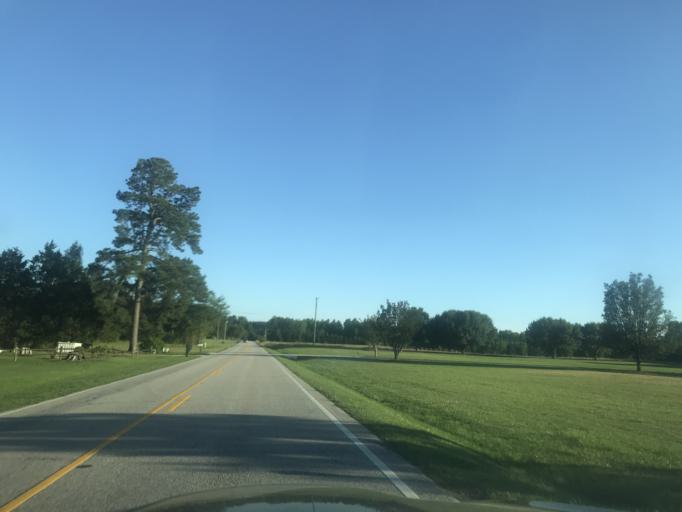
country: US
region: North Carolina
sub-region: Johnston County
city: Archer Lodge
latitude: 35.7131
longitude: -78.3853
